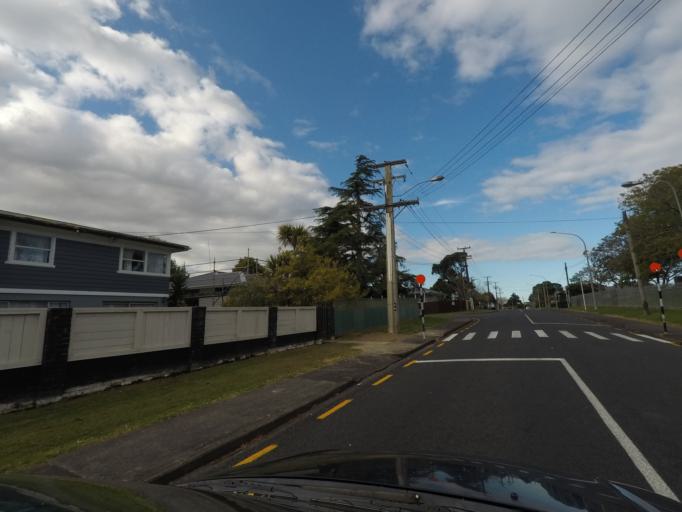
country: NZ
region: Auckland
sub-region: Auckland
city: Rosebank
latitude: -36.8869
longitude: 174.6545
